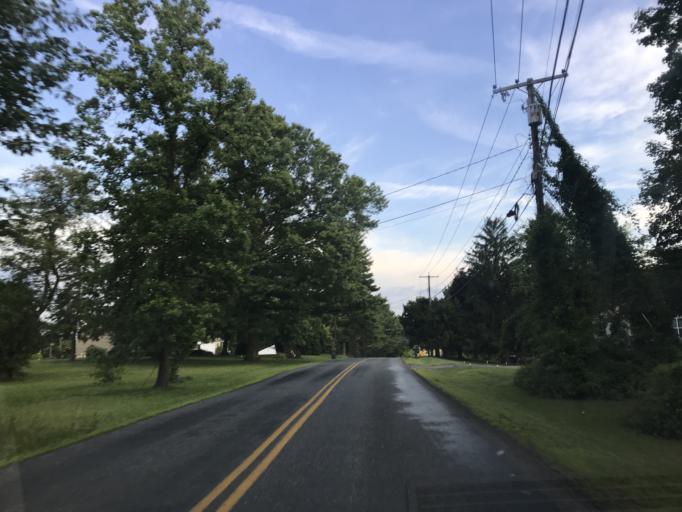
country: US
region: Maryland
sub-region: Harford County
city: Perryman
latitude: 39.5068
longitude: -76.2065
